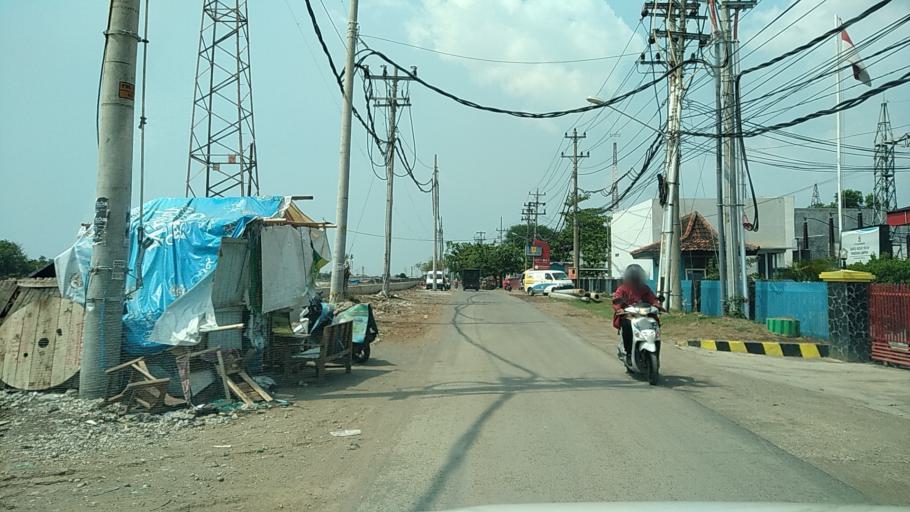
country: ID
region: Central Java
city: Semarang
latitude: -6.9940
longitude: 110.4403
